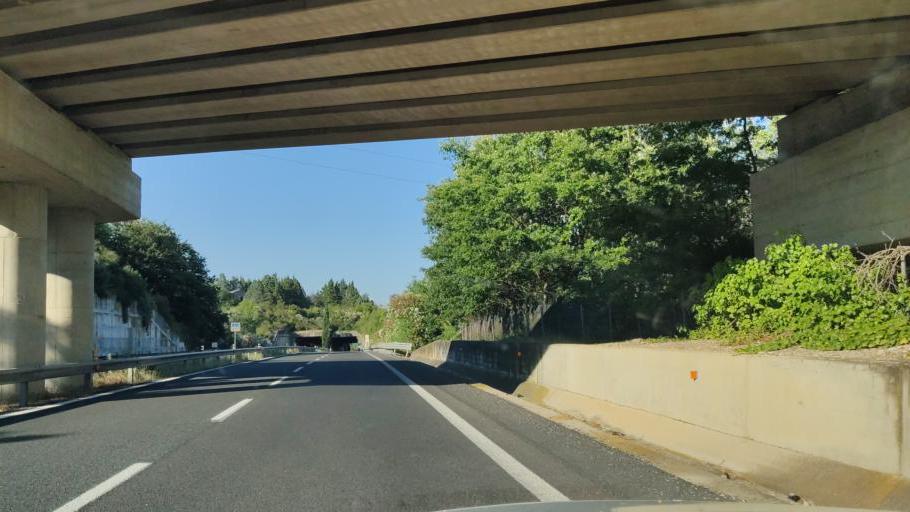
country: IT
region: Latium
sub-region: Provincia di Viterbo
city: Orte Scalo
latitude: 42.4585
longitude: 12.4105
